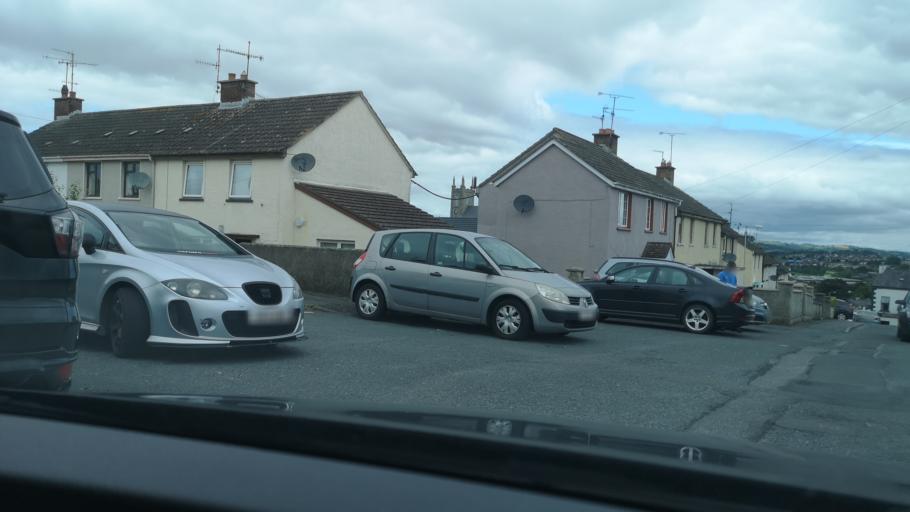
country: GB
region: Northern Ireland
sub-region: Newry and Mourne District
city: Newry
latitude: 54.1757
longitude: -6.3285
